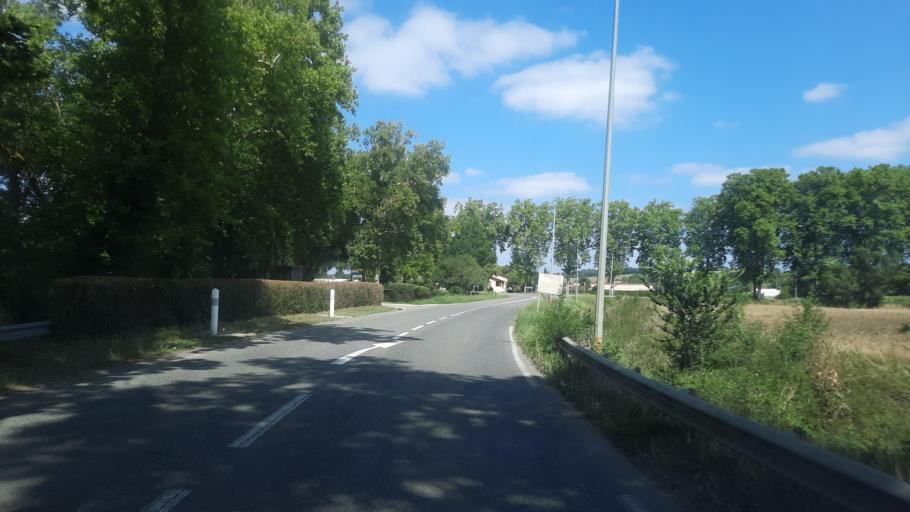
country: FR
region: Midi-Pyrenees
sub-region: Departement du Gers
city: Samatan
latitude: 43.4860
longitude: 0.9331
